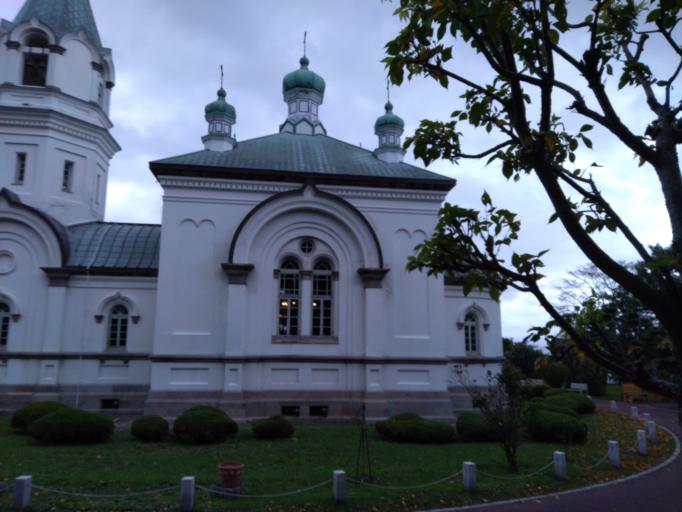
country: JP
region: Hokkaido
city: Hakodate
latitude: 41.7627
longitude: 140.7120
